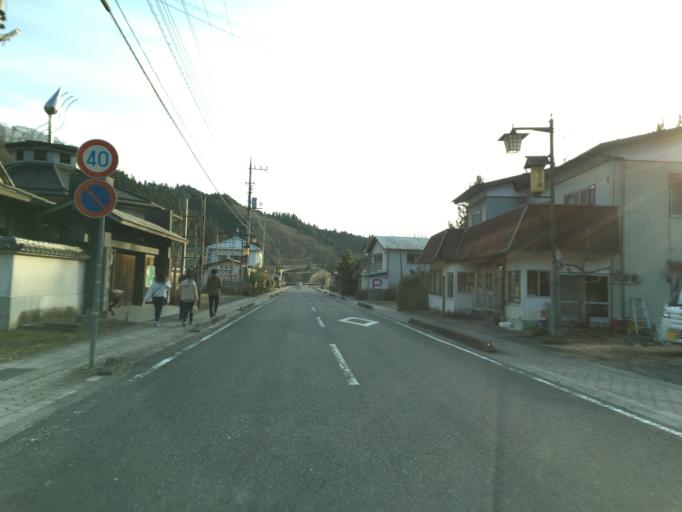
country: JP
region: Ibaraki
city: Daigo
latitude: 36.7627
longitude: 140.3982
